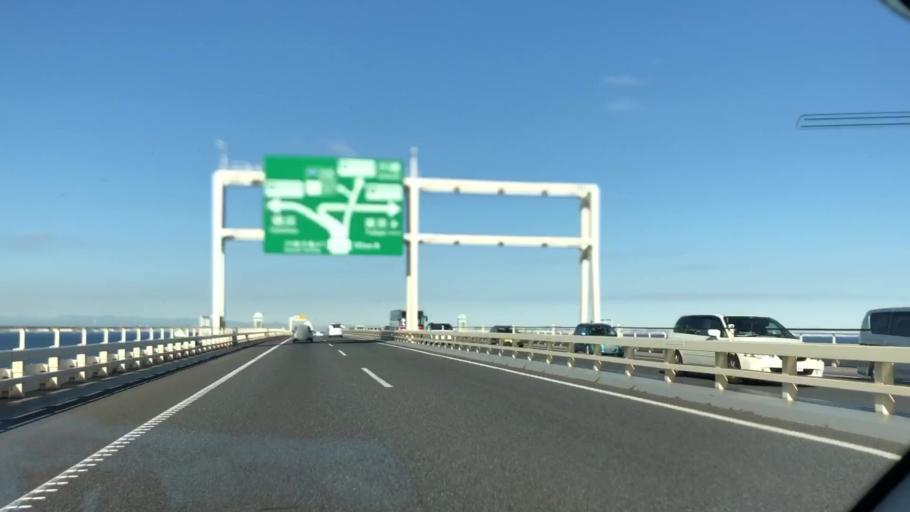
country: JP
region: Chiba
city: Kisarazu
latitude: 35.4552
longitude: 139.8877
